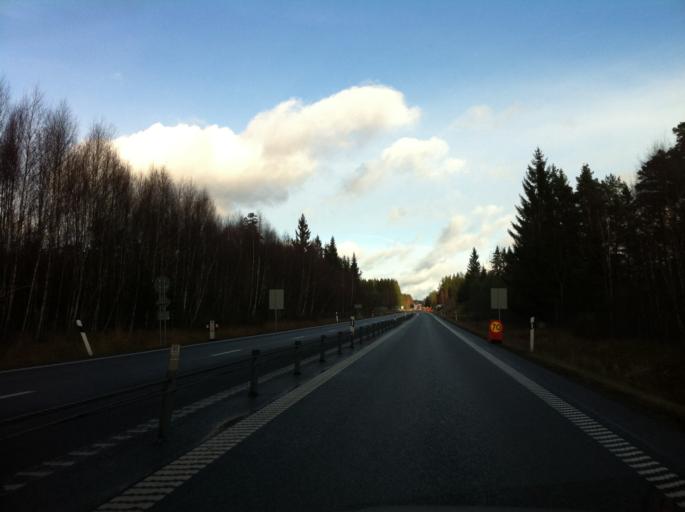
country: SE
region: Skane
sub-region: Osby Kommun
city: Osby
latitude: 56.4123
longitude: 14.0476
